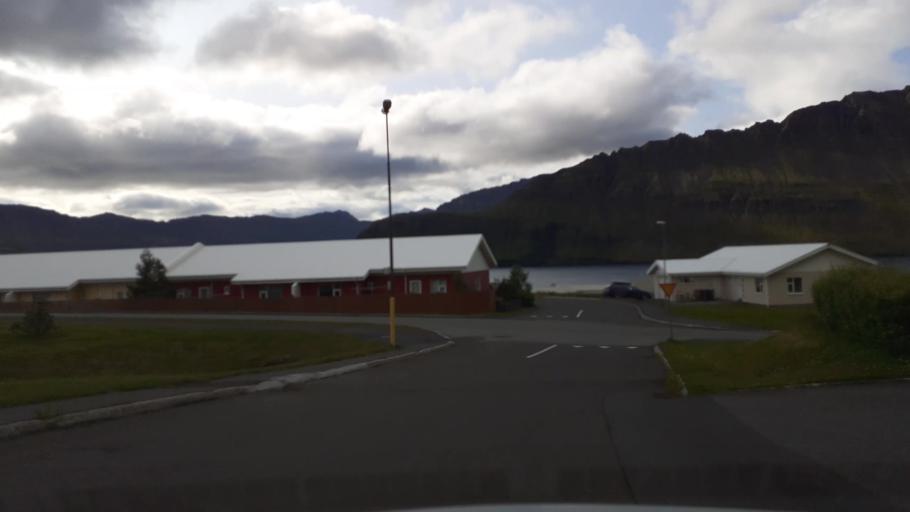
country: IS
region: East
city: Neskaupstadur
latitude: 65.1487
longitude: -13.6706
